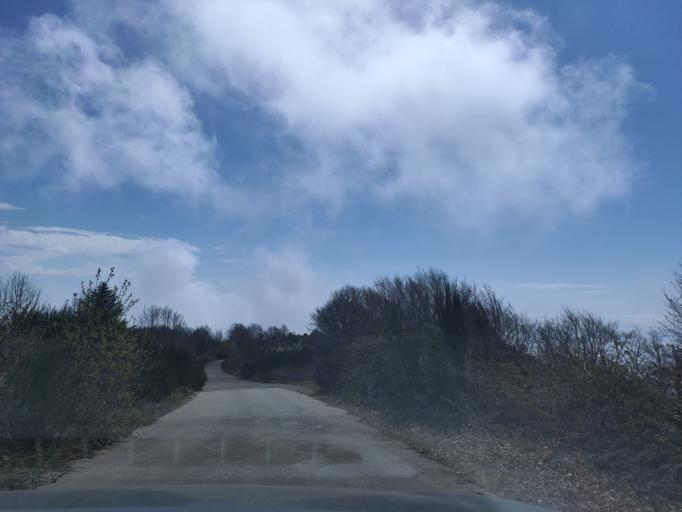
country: ES
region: Catalonia
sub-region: Provincia de Barcelona
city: Fogars de Montclus
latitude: 41.7642
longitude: 2.4556
